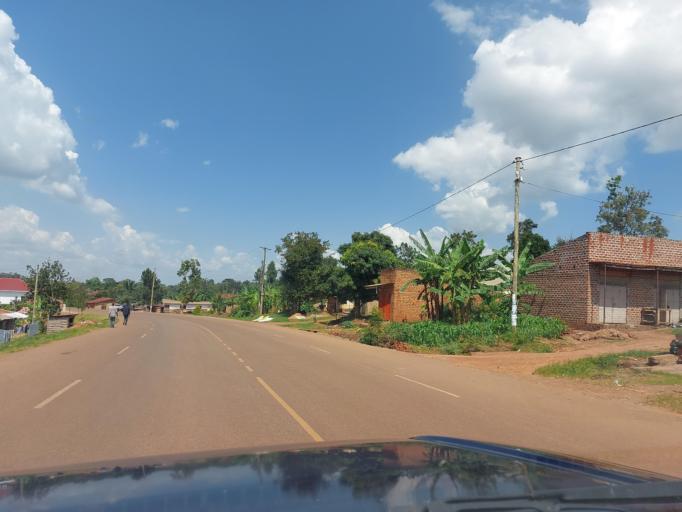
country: UG
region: Central Region
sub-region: Buikwe District
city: Njeru
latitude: 0.3872
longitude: 33.1644
